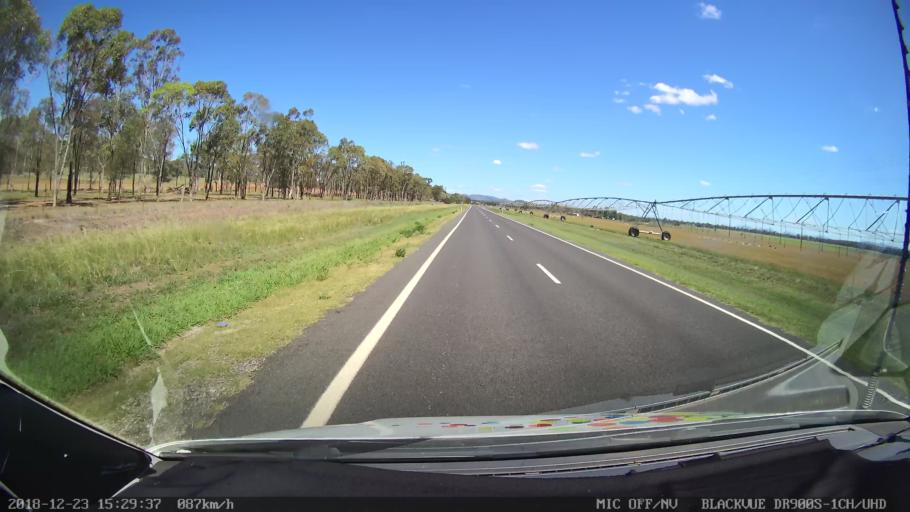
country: AU
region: New South Wales
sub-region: Tamworth Municipality
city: East Tamworth
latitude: -30.9487
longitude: 150.8620
